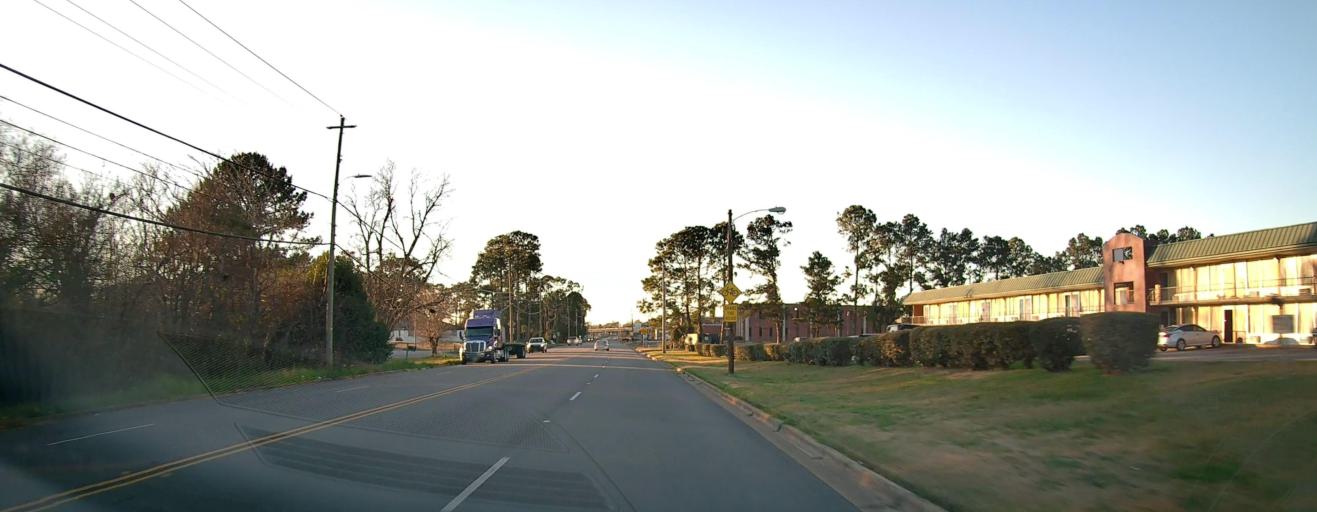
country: US
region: Georgia
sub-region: Dougherty County
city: Albany
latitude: 31.6126
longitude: -84.1776
